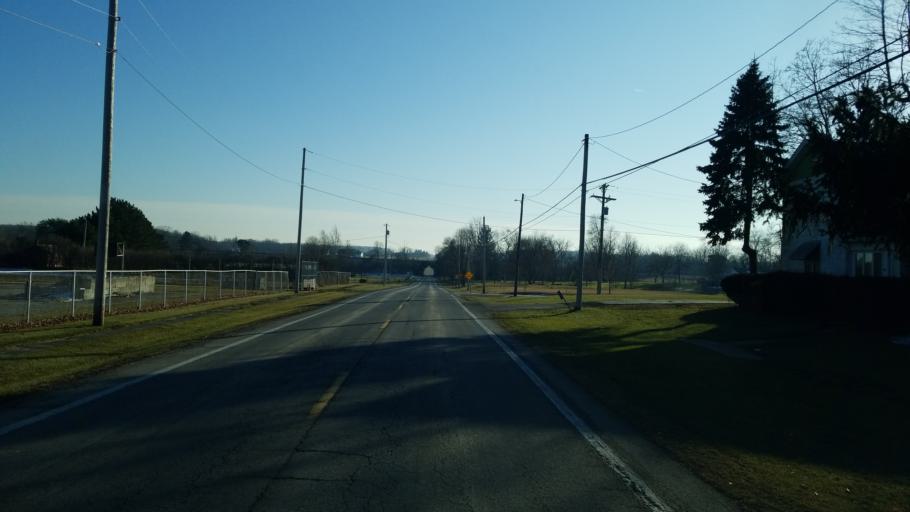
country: US
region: Ohio
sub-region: Sandusky County
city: Green Springs
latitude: 41.1206
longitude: -83.0155
